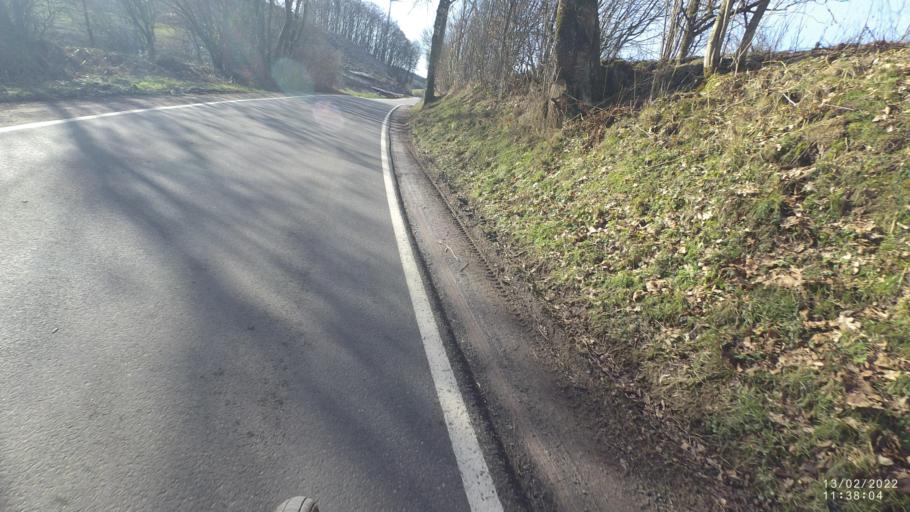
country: DE
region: North Rhine-Westphalia
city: Neuenrade
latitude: 51.3185
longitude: 7.7724
